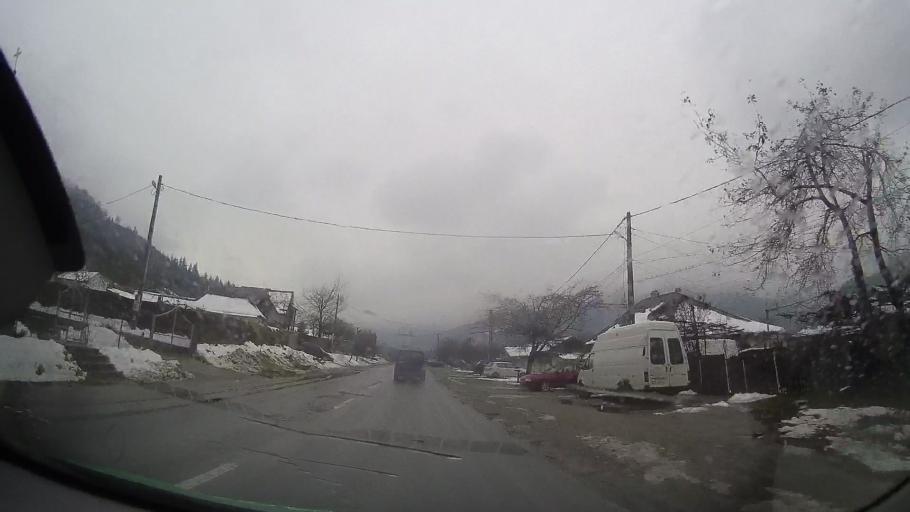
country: RO
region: Neamt
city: Viisoara
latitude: 46.9282
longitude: 26.2298
